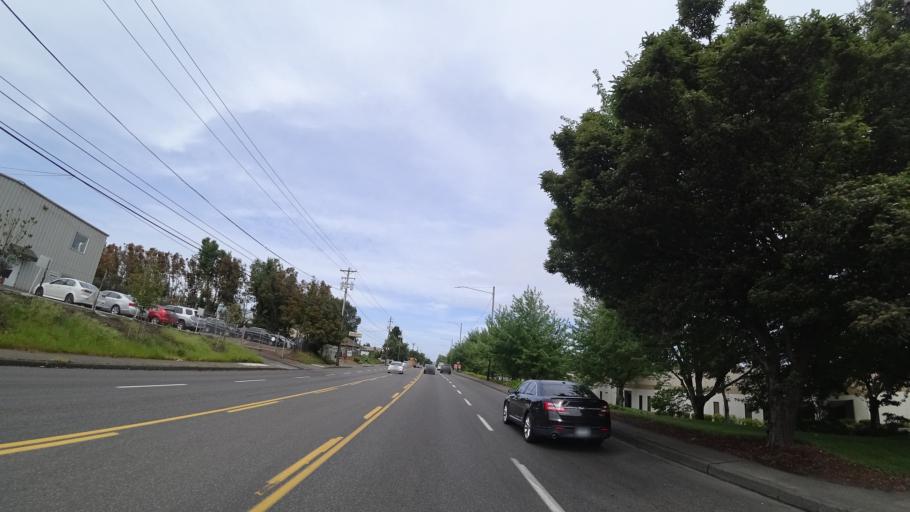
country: US
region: Oregon
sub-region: Multnomah County
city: Portland
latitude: 45.5689
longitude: -122.6015
